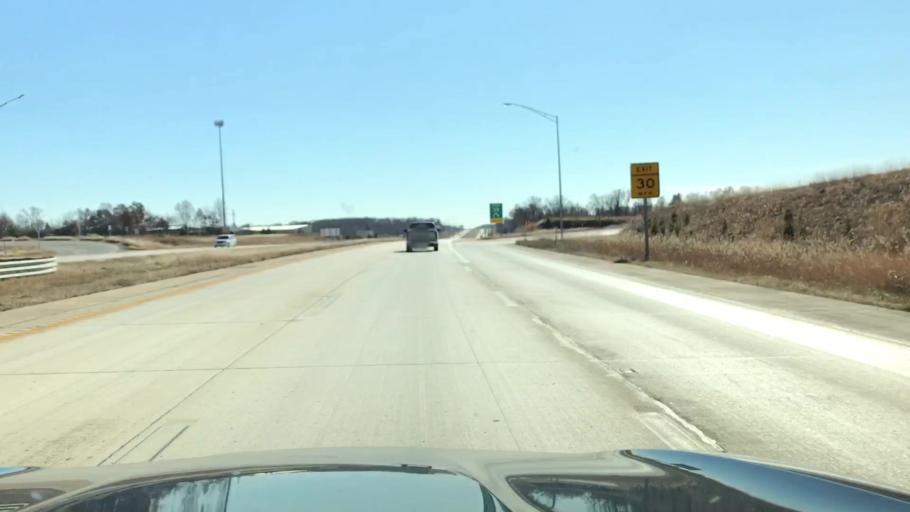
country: US
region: Missouri
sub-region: Jasper County
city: Duenweg
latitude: 37.0544
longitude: -94.4266
